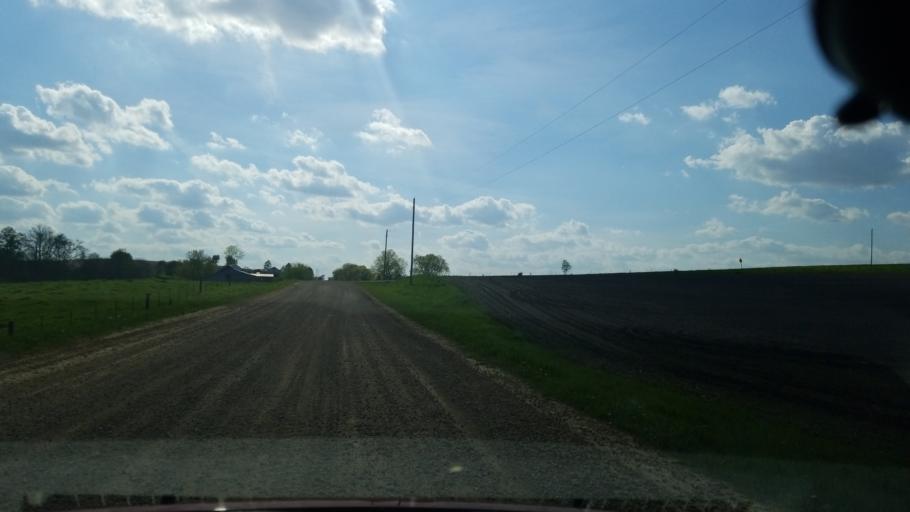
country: US
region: Iowa
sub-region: Jackson County
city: Maquoketa
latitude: 42.2149
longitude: -90.6930
